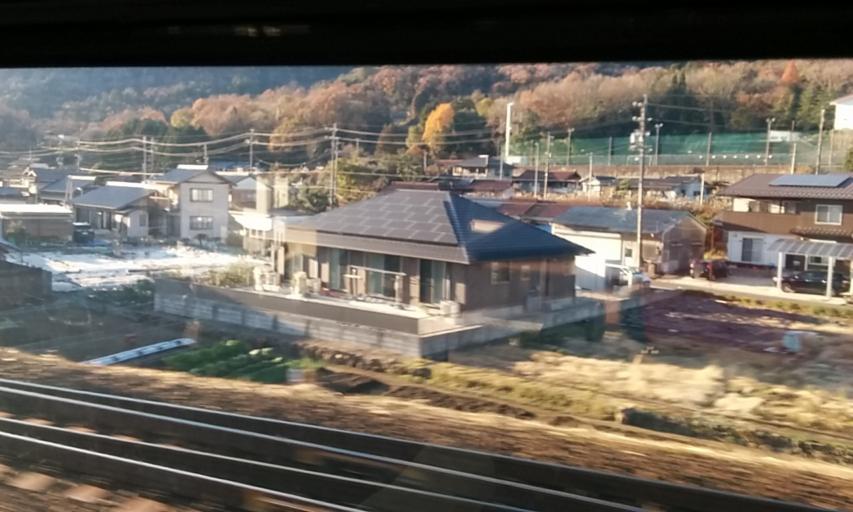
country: JP
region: Gifu
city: Mizunami
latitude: 35.4090
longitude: 137.3027
